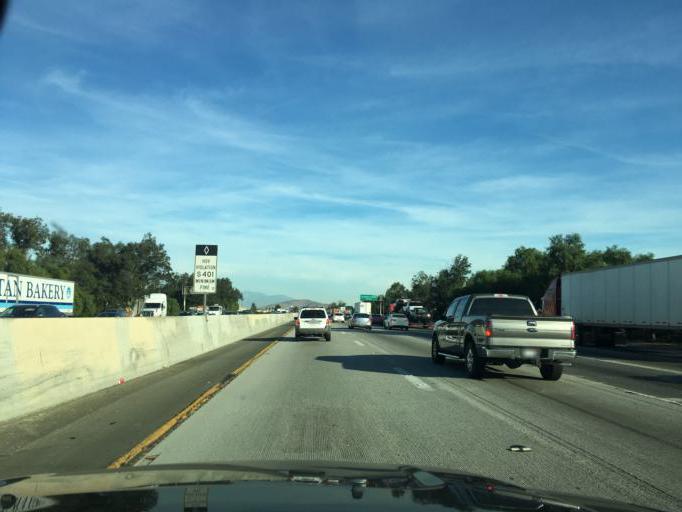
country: US
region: California
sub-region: San Bernardino County
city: Ontario
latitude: 34.0305
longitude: -117.6130
